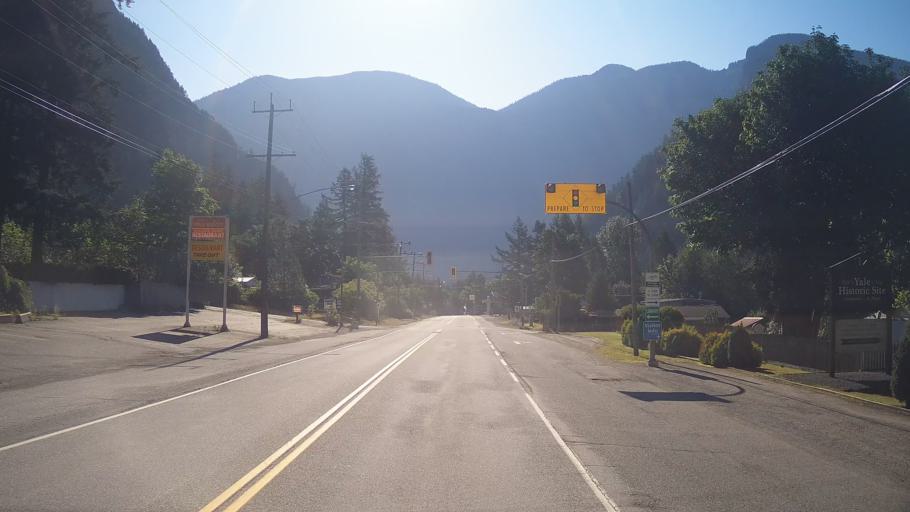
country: CA
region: British Columbia
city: Hope
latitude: 49.5632
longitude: -121.4322
